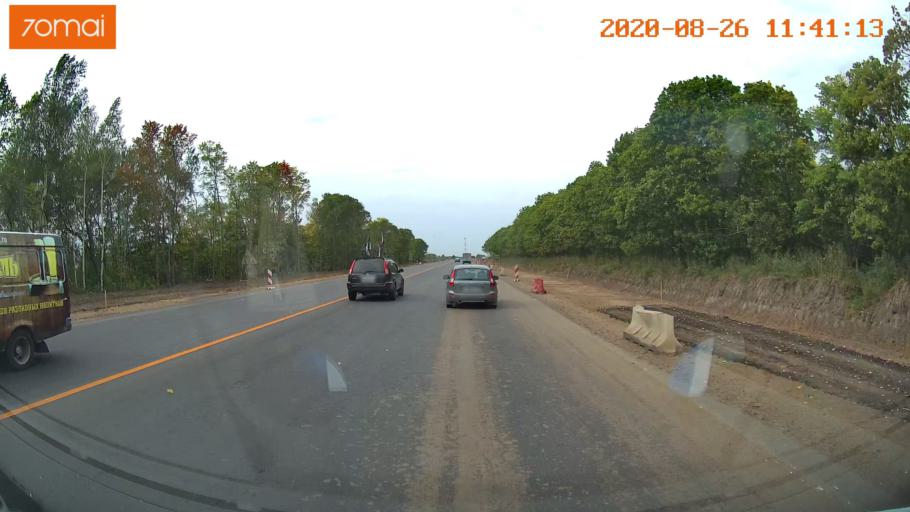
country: RU
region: Rjazan
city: Shilovo
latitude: 54.2951
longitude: 40.7154
